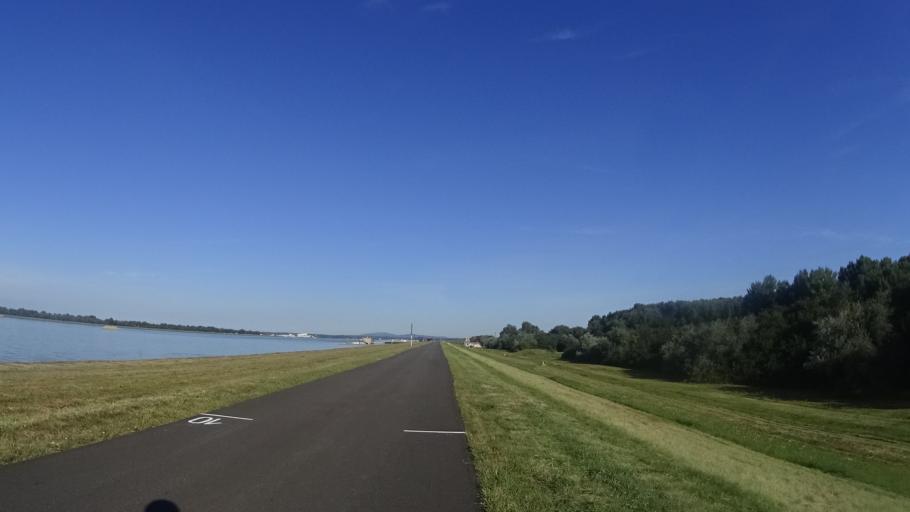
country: SK
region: Bratislavsky
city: Dunajska Luzna
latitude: 48.0301
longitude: 17.2554
